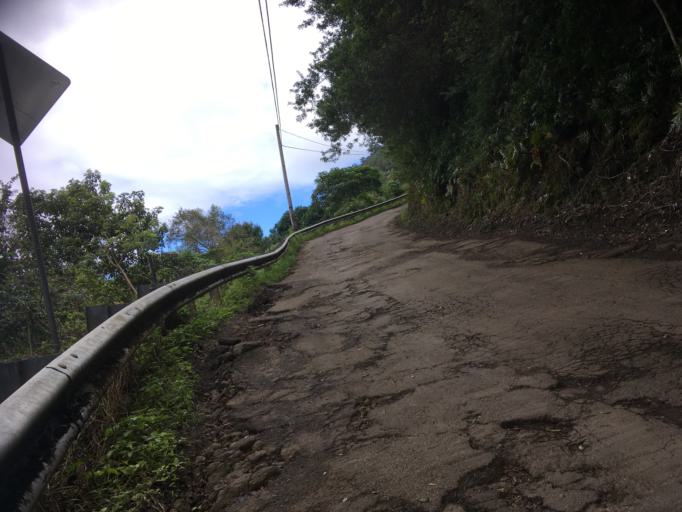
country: US
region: Hawaii
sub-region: Hawaii County
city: Waimea
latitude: 20.1135
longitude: -155.5928
